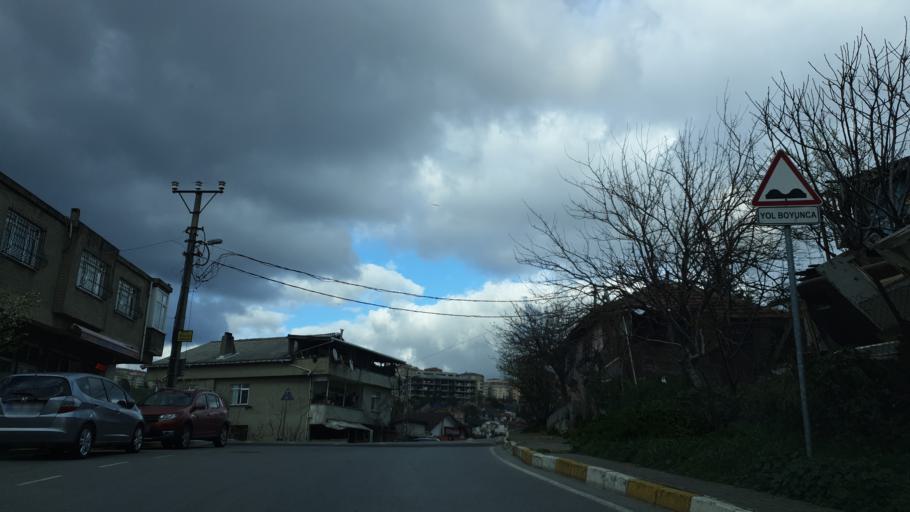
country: TR
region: Istanbul
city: Pendik
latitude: 40.8987
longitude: 29.2376
